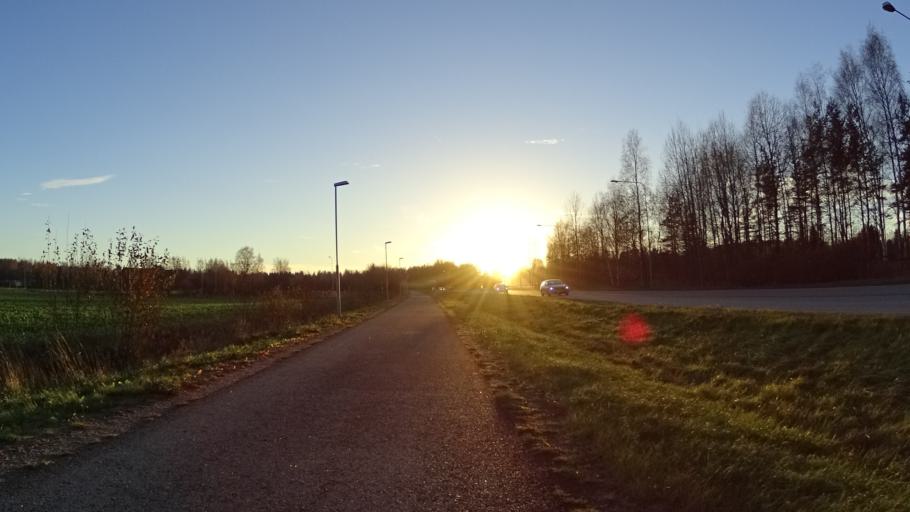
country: FI
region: Uusimaa
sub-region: Helsinki
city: Vantaa
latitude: 60.2613
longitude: 24.9658
